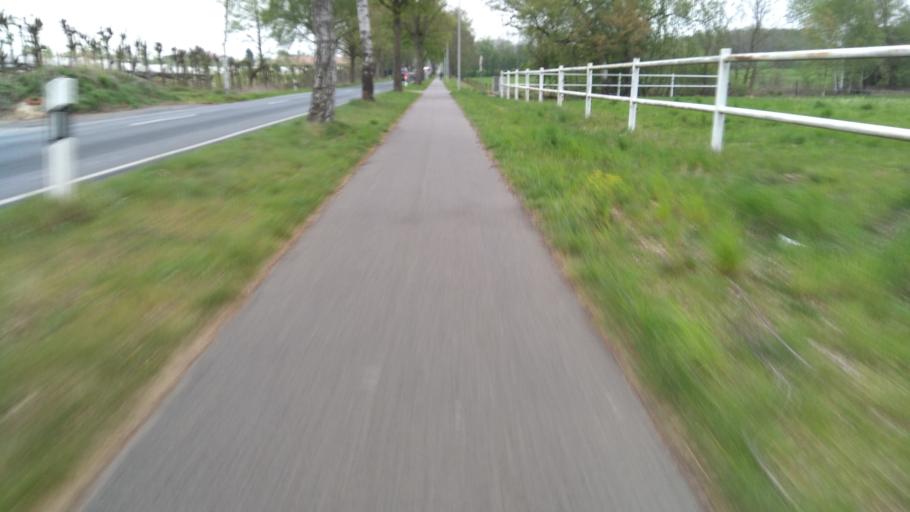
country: DE
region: Lower Saxony
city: Apensen
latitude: 53.4495
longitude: 9.6421
